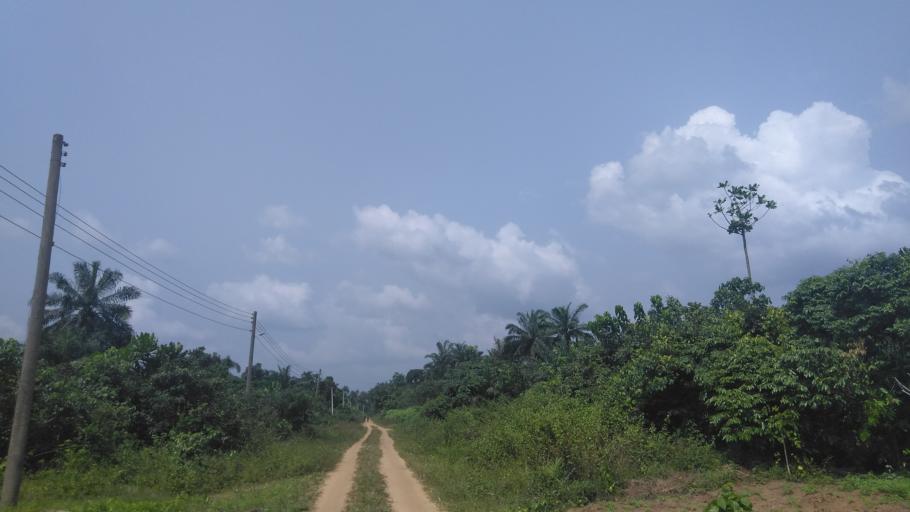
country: NG
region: Abia
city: Aba
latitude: 5.0421
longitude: 7.2368
